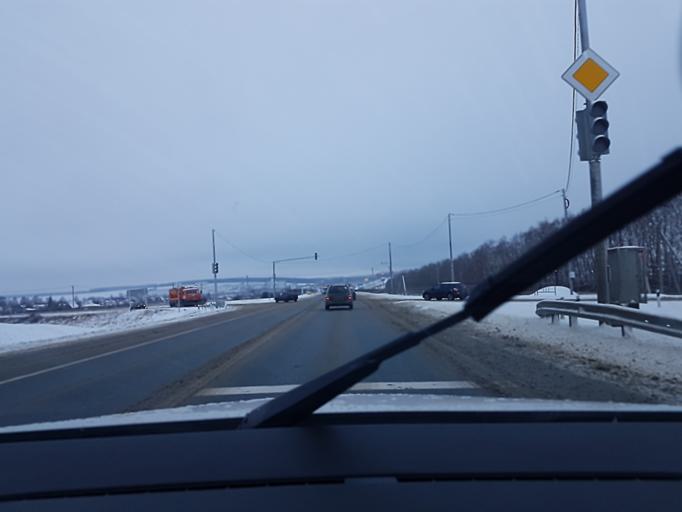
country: RU
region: Moskovskaya
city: Uzunovo
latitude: 54.4677
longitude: 38.5456
